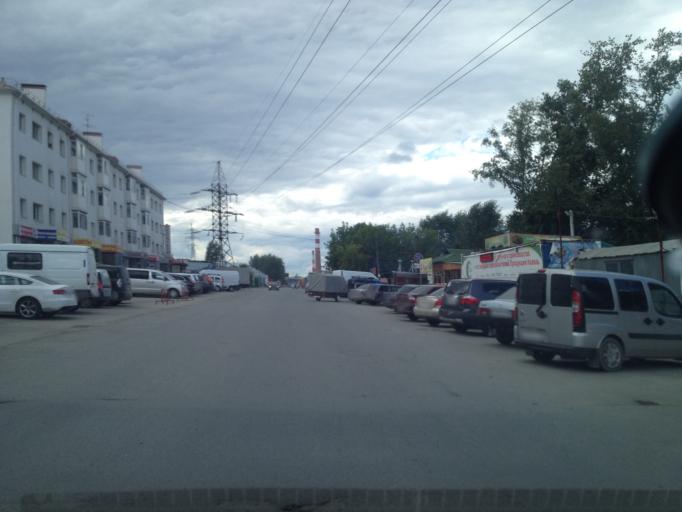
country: RU
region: Sverdlovsk
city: Yekaterinburg
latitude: 56.8620
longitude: 60.5366
